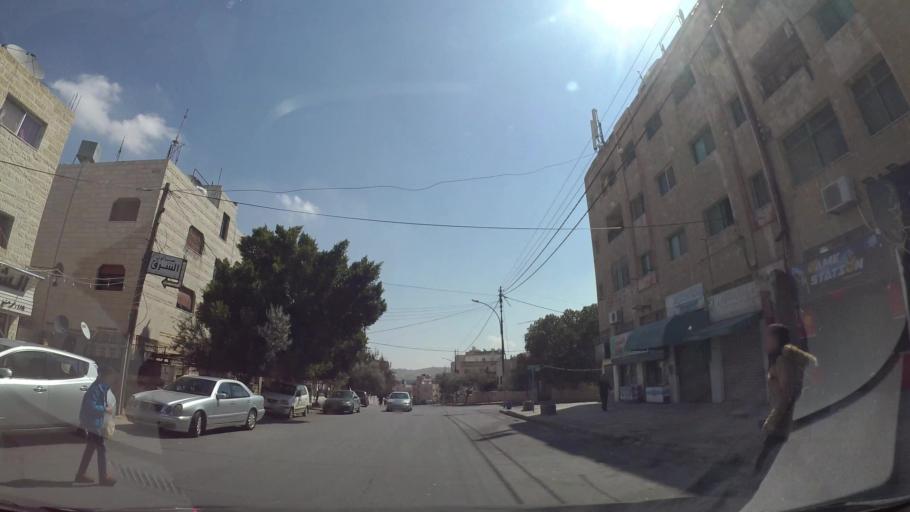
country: JO
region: Amman
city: Amman
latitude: 31.9771
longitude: 35.9873
